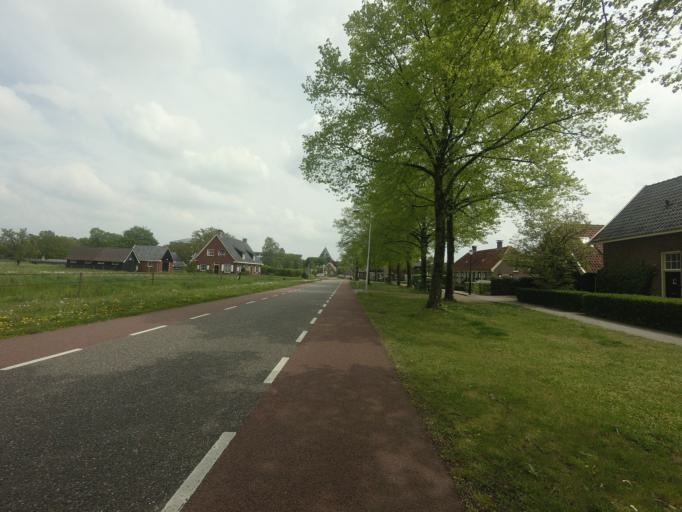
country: NL
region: Overijssel
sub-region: Gemeente Hof van Twente
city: Delden
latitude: 52.2651
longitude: 6.7062
